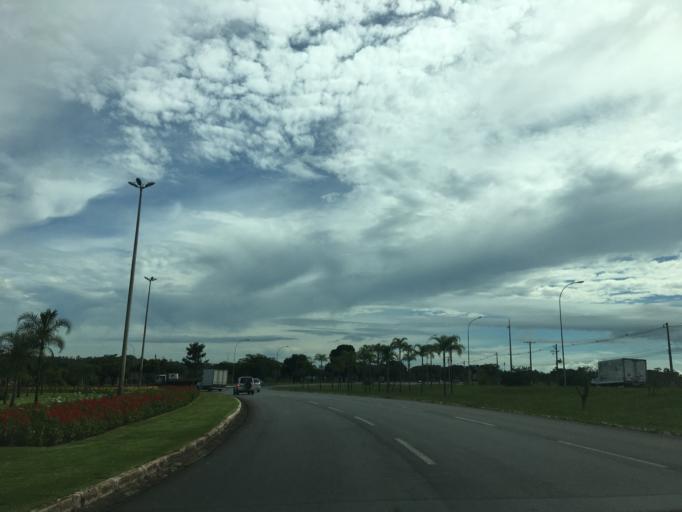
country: BR
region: Federal District
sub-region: Brasilia
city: Brasilia
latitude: -15.8617
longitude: -47.9346
